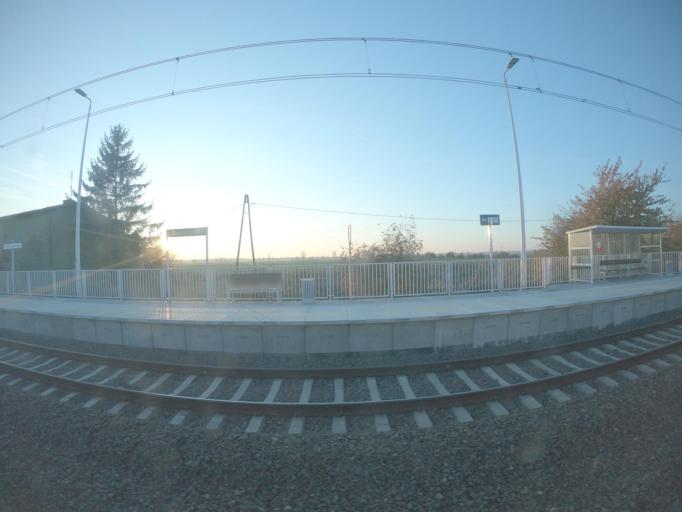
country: PL
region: Lubusz
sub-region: Powiat slubicki
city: Gorzyca
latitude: 52.5154
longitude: 14.6510
